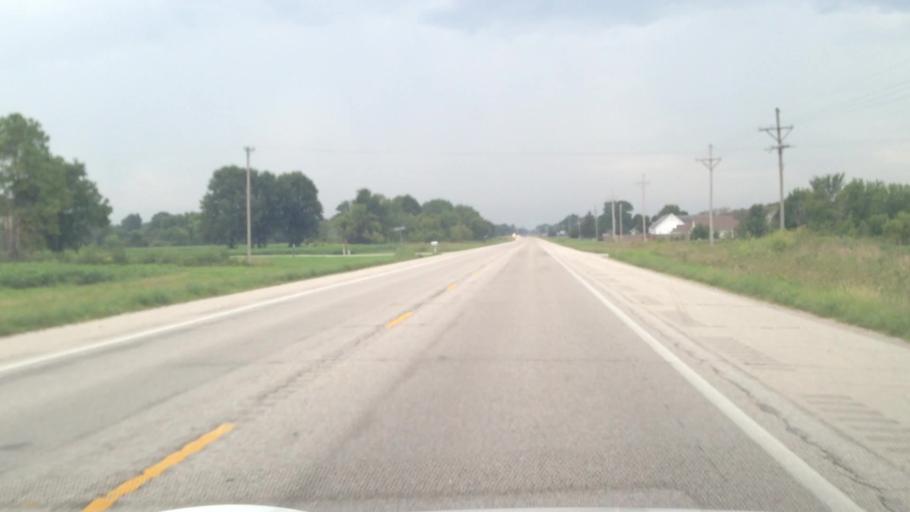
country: US
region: Kansas
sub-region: Cherokee County
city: Galena
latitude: 37.0977
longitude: -94.7045
